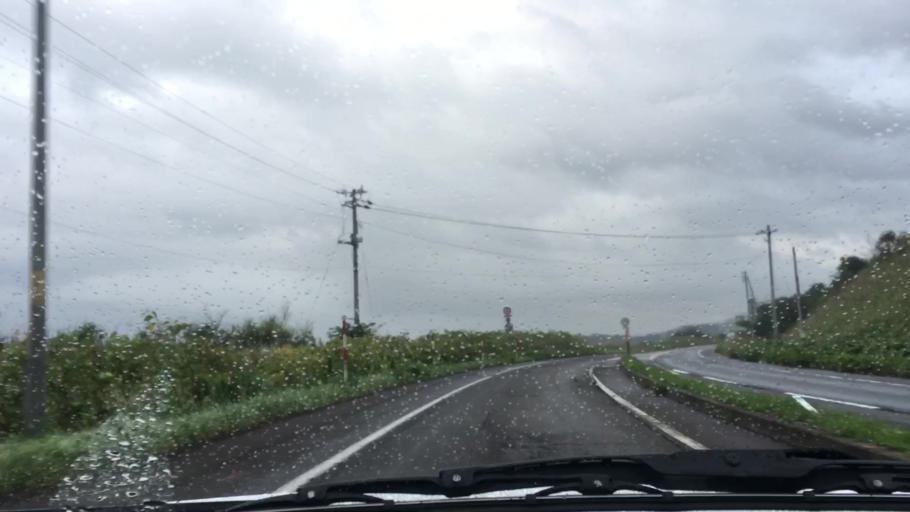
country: JP
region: Hokkaido
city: Nanae
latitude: 42.1873
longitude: 140.4356
